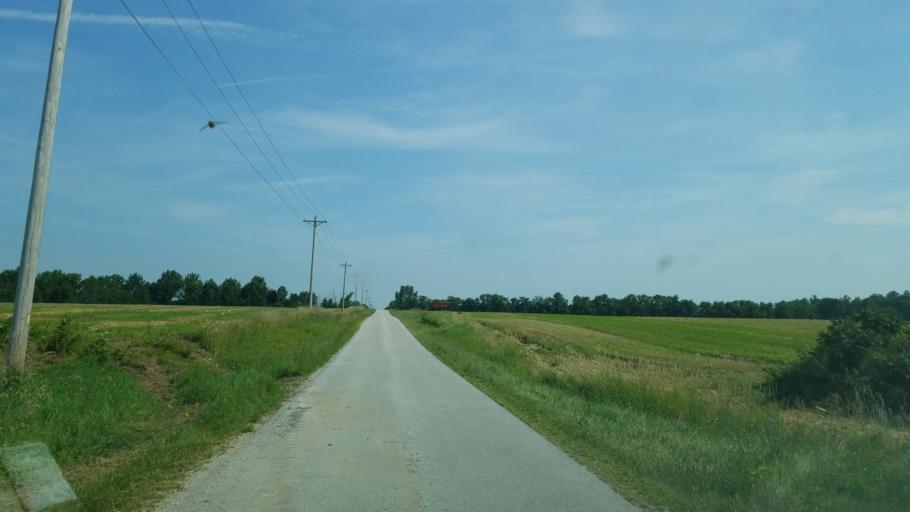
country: US
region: Ohio
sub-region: Sandusky County
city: Green Springs
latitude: 41.1279
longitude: -82.9961
